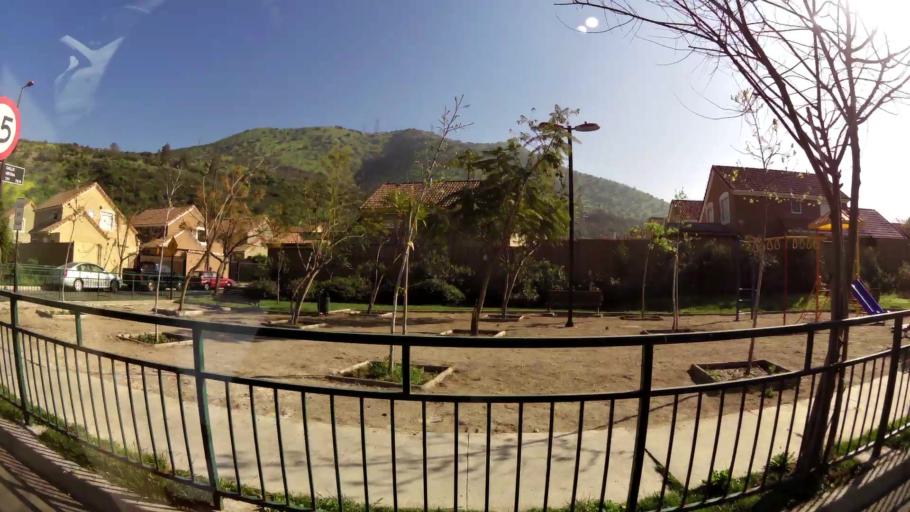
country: CL
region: Santiago Metropolitan
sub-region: Provincia de Chacabuco
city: Chicureo Abajo
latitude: -33.3462
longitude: -70.6776
